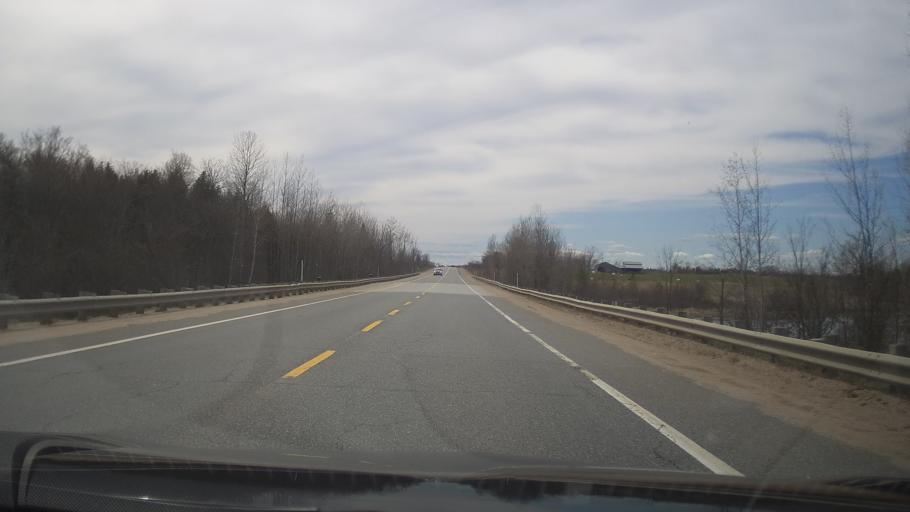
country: CA
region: Ontario
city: Arnprior
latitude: 45.5274
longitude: -76.2274
